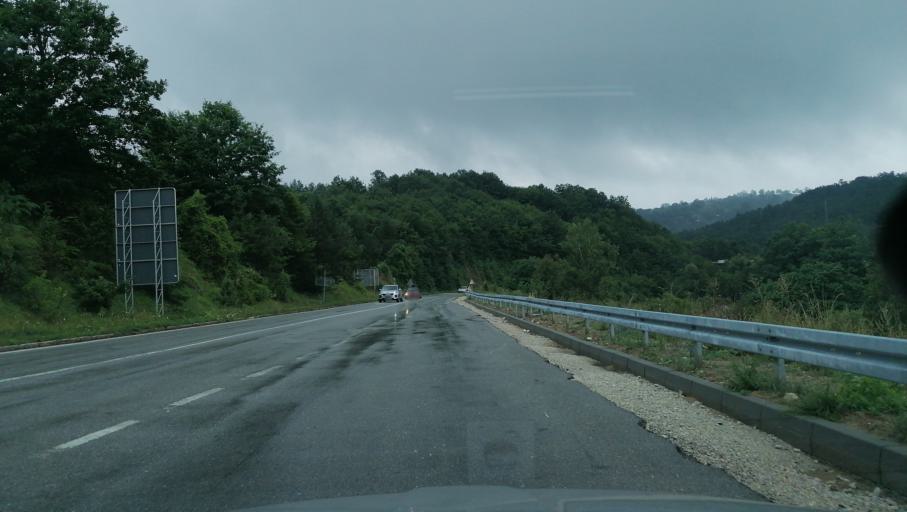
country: RS
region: Central Serbia
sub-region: Zlatiborski Okrug
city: Cajetina
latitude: 43.7841
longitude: 19.7370
